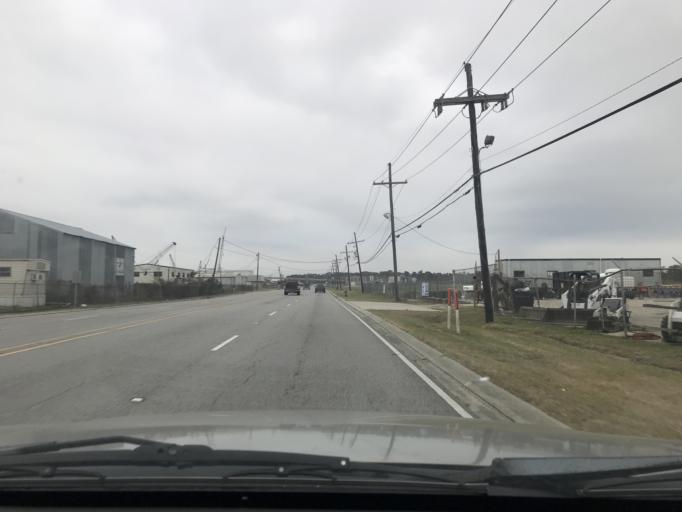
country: US
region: Louisiana
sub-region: Jefferson Parish
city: Woodmere
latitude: 29.8782
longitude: -90.0747
